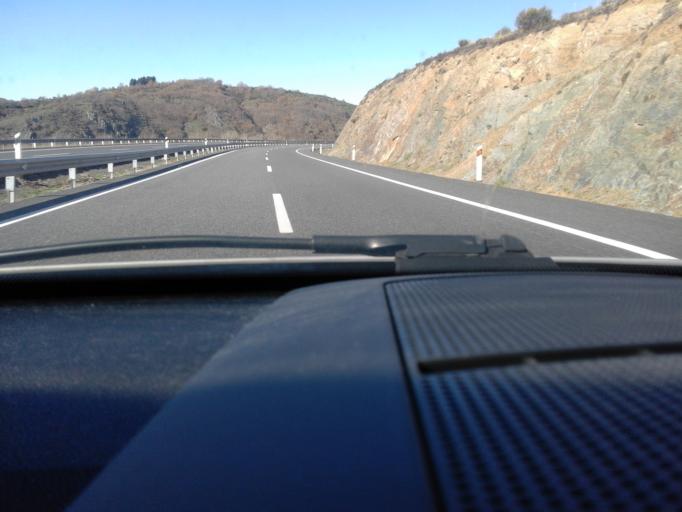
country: ES
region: Castille and Leon
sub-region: Provincia de Leon
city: Carrocera
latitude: 42.7678
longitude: -5.7784
